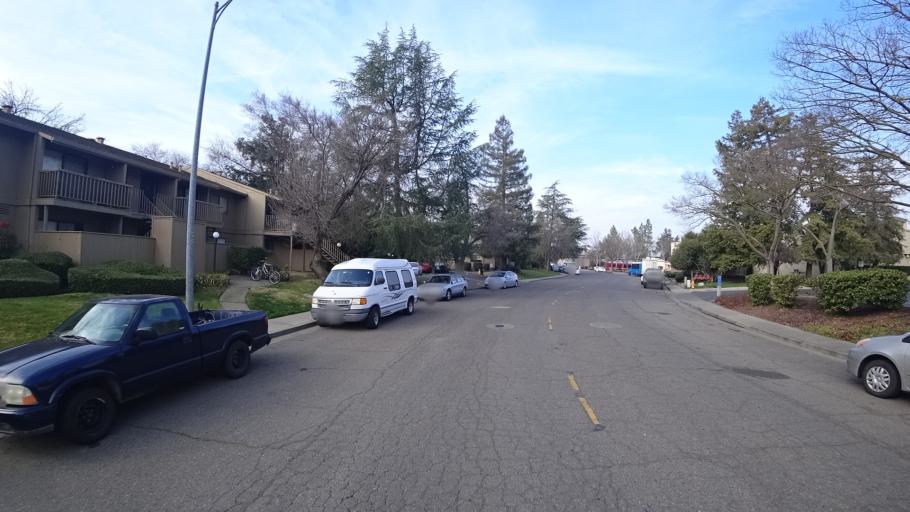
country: US
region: California
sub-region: Yolo County
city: Davis
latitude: 38.5589
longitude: -121.7570
